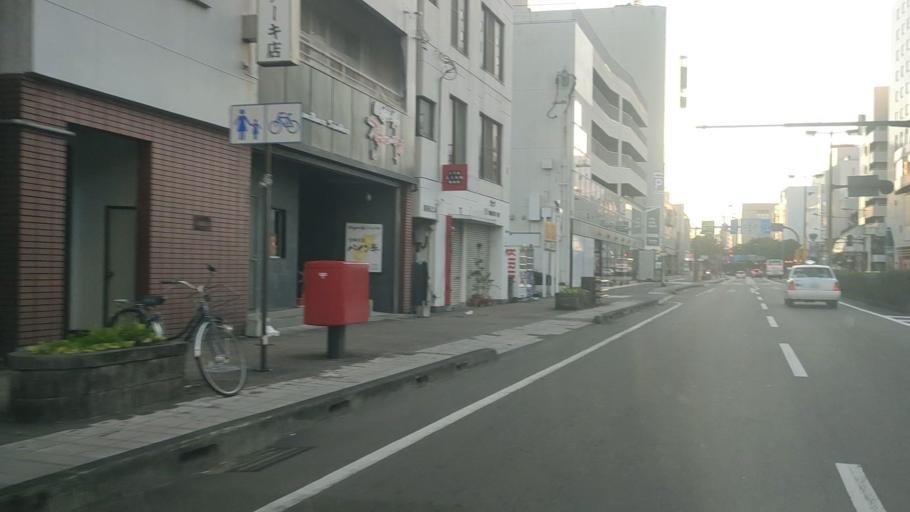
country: JP
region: Miyazaki
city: Miyazaki-shi
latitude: 31.9171
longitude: 131.4211
